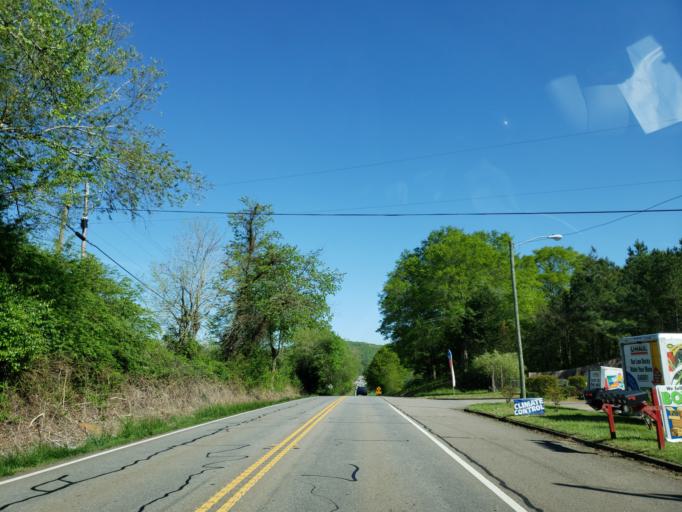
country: US
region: Georgia
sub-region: Cherokee County
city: Canton
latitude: 34.3066
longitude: -84.5288
